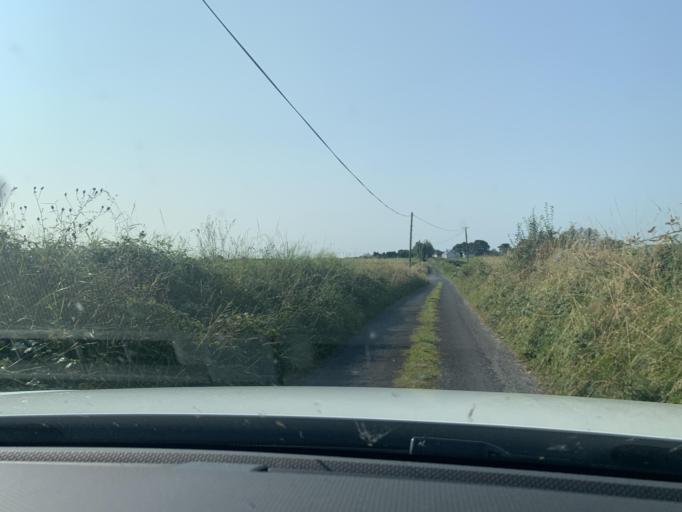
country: IE
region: Connaught
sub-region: Maigh Eo
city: Ballyhaunis
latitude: 53.7889
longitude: -8.7387
